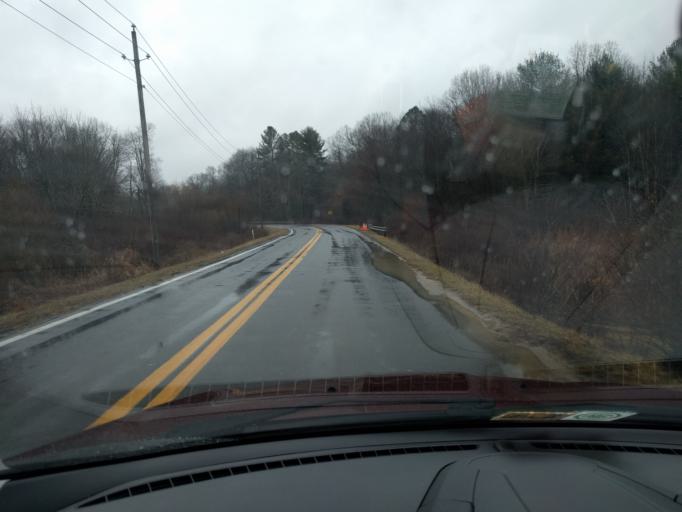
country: US
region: West Virginia
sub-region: Raleigh County
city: Beckley
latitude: 37.7939
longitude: -81.1949
